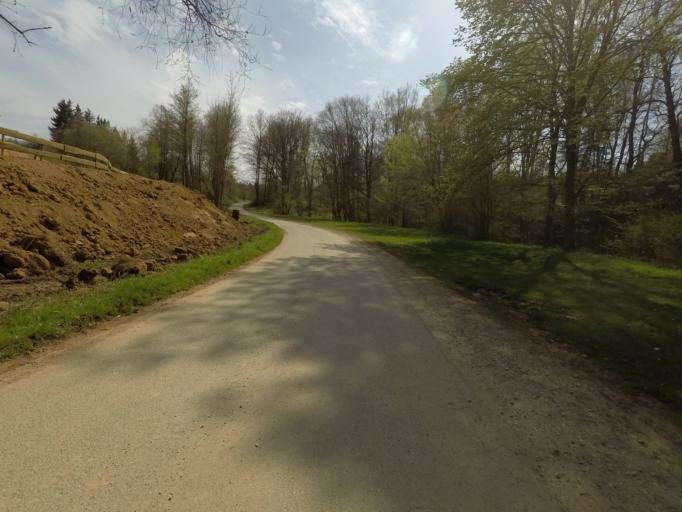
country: DE
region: Baden-Wuerttemberg
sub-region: Tuebingen Region
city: Reutlingen
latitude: 48.4766
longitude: 9.1753
